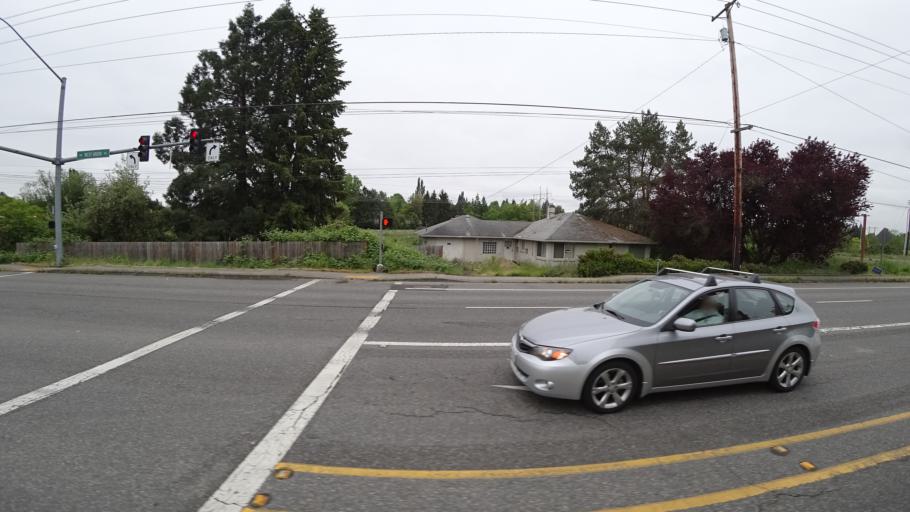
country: US
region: Oregon
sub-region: Washington County
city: Bethany
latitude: 45.5578
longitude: -122.8657
